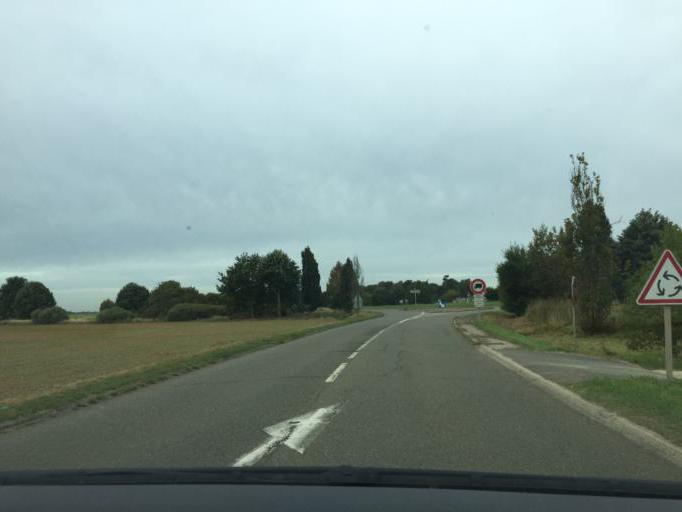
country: FR
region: Ile-de-France
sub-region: Departement de l'Essonne
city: Villiers-le-Bacle
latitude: 48.7417
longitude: 2.1208
